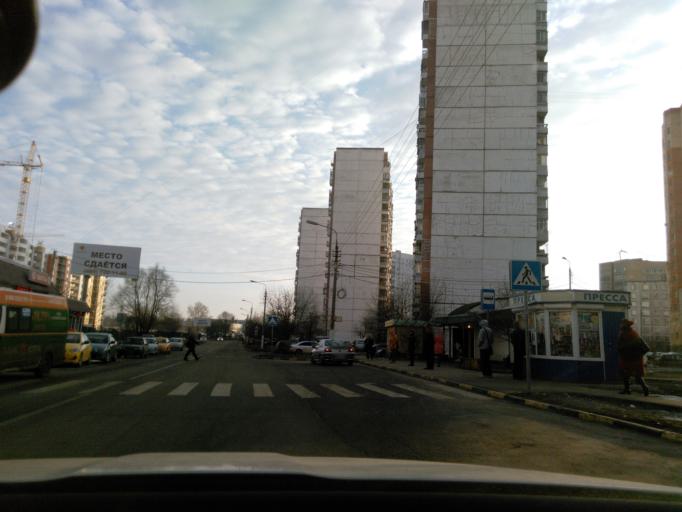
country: RU
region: Moscow
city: Khimki
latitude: 55.9038
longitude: 37.4041
